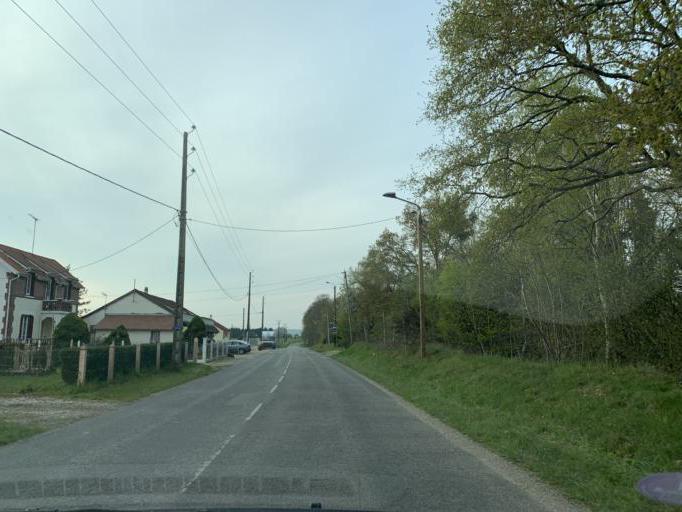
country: FR
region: Haute-Normandie
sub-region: Departement de la Seine-Maritime
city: La Mailleraye-sur-Seine
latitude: 49.4878
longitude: 0.7688
